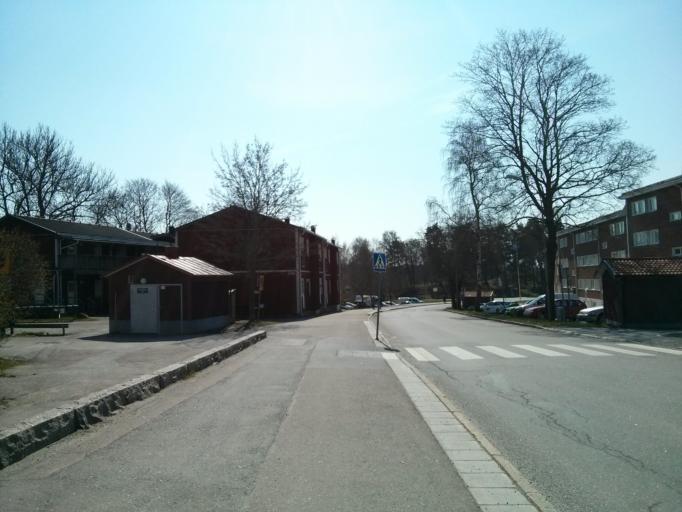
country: SE
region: Stockholm
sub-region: Upplands Vasby Kommun
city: Upplands Vaesby
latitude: 59.5189
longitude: 17.8941
